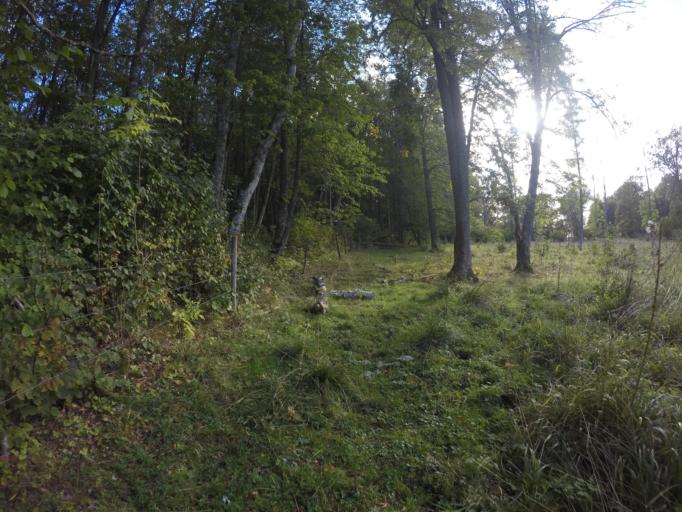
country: SE
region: Vaestmanland
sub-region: Hallstahammars Kommun
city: Kolback
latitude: 59.4805
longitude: 16.2282
